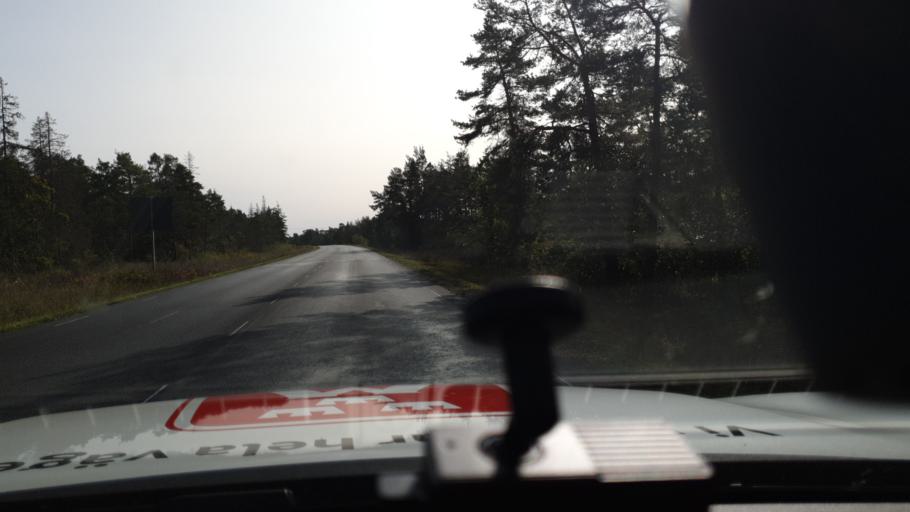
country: SE
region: Gotland
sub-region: Gotland
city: Slite
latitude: 57.7489
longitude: 18.7896
